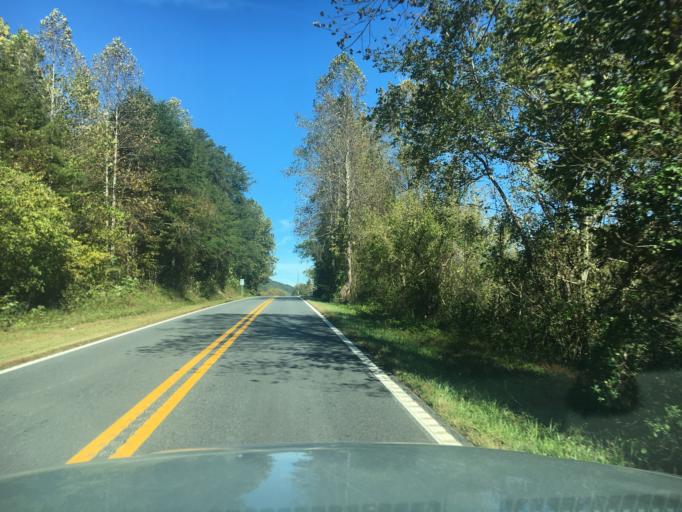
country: US
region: North Carolina
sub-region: Rutherford County
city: Spindale
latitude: 35.5229
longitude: -81.8552
